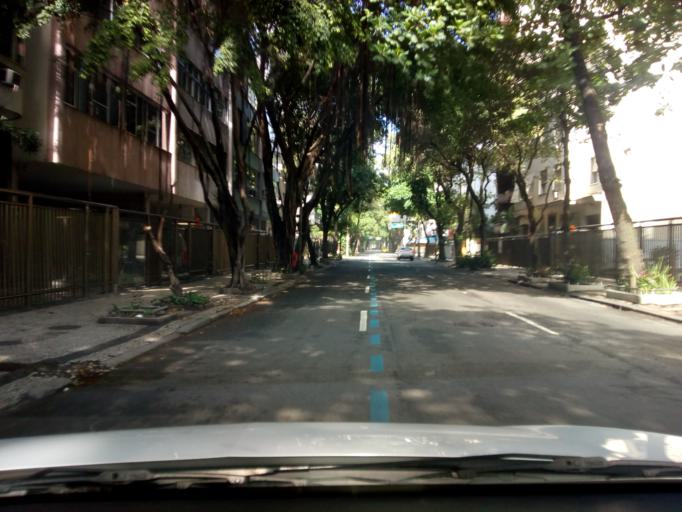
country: BR
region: Rio de Janeiro
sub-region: Rio De Janeiro
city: Rio de Janeiro
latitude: -22.9854
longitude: -43.2015
